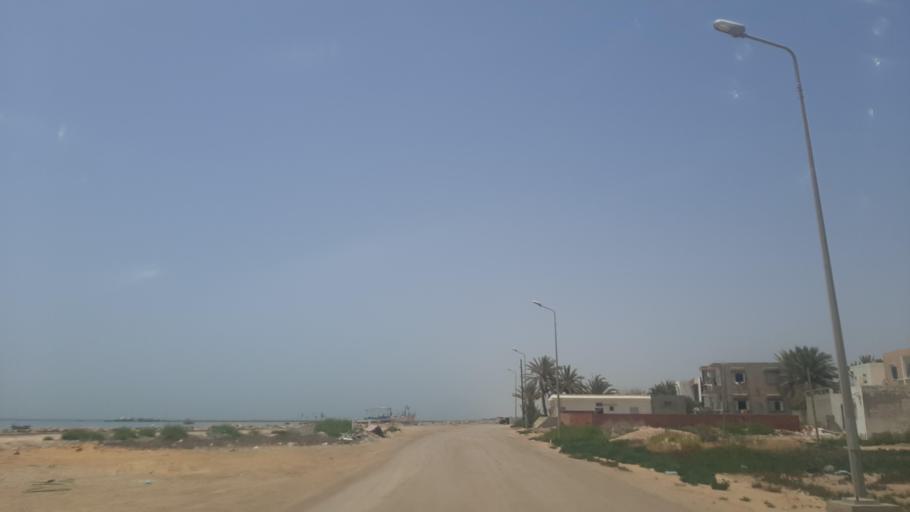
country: TN
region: Safaqis
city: Al Qarmadah
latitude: 34.7001
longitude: 11.1976
